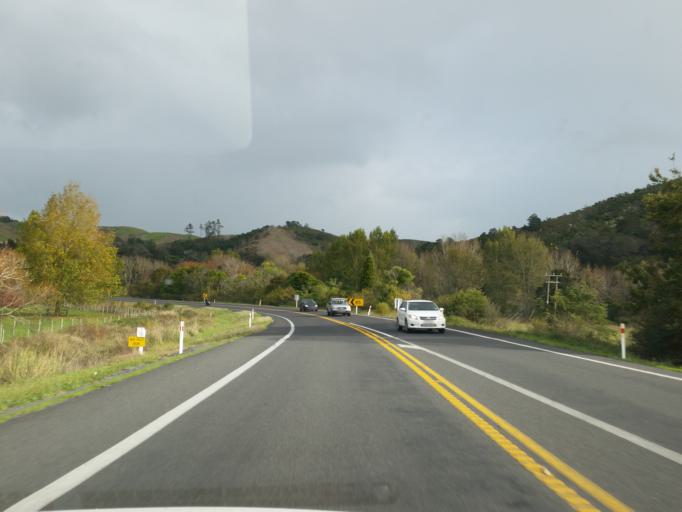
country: NZ
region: Waikato
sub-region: Hauraki District
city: Paeroa
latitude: -37.4086
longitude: 175.7060
